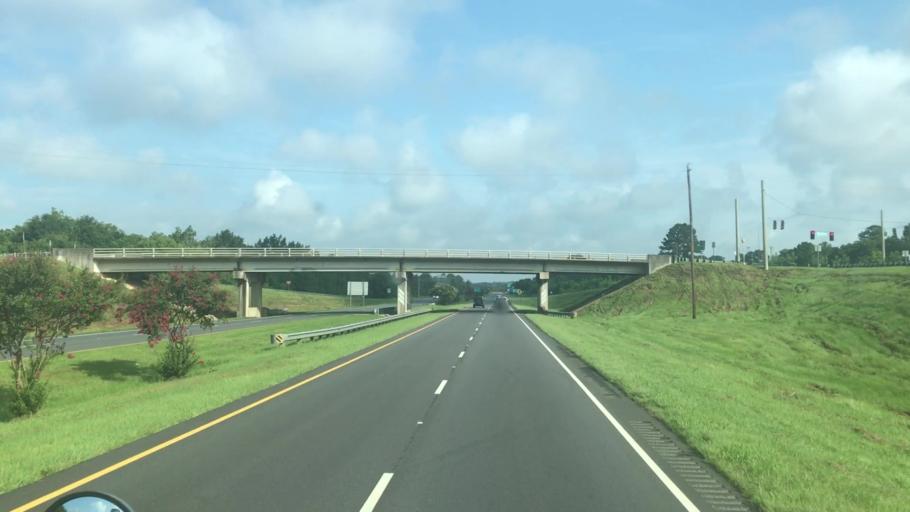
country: US
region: Georgia
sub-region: Decatur County
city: Bainbridge
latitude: 30.9108
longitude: -84.5933
